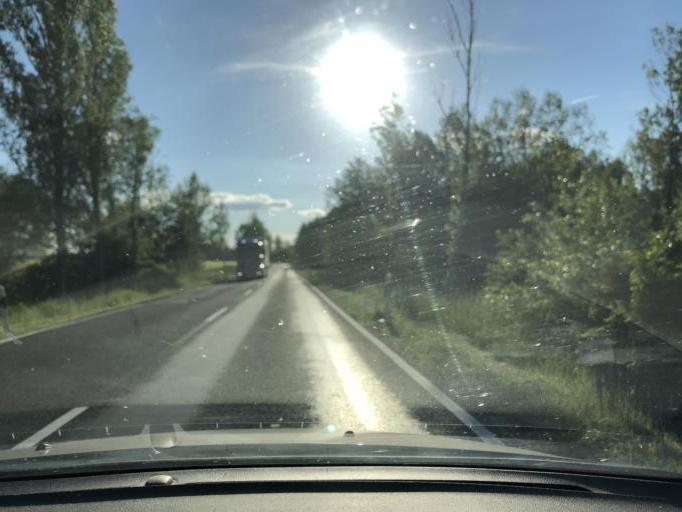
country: DE
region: Thuringia
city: Lucka
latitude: 51.0835
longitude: 12.3115
